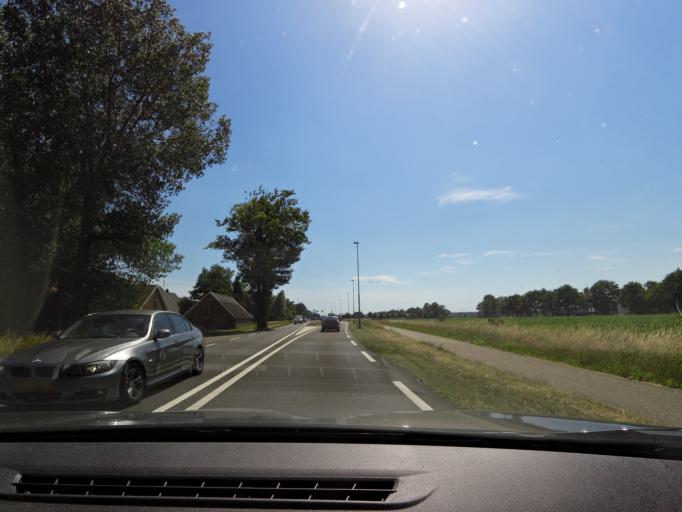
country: NL
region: Gelderland
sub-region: Berkelland
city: Eibergen
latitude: 52.0635
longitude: 6.6304
